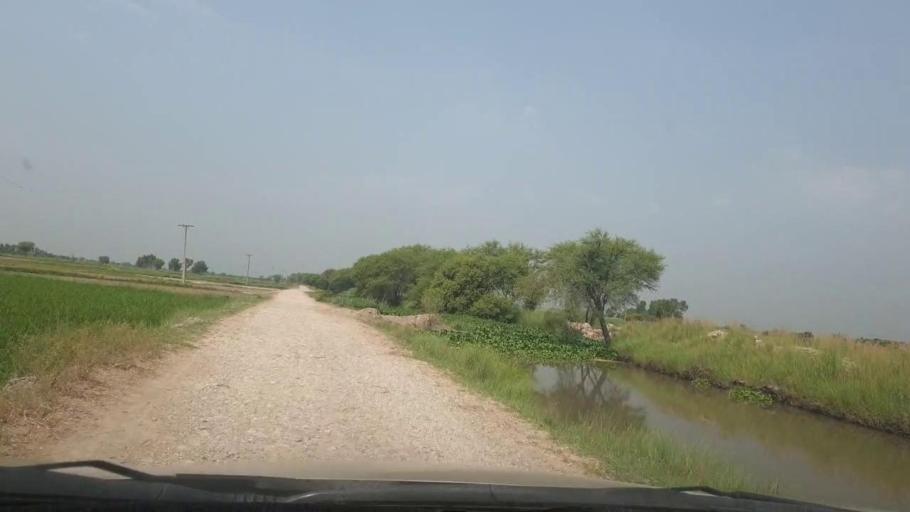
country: PK
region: Sindh
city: Ratodero
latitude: 27.6886
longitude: 68.2406
